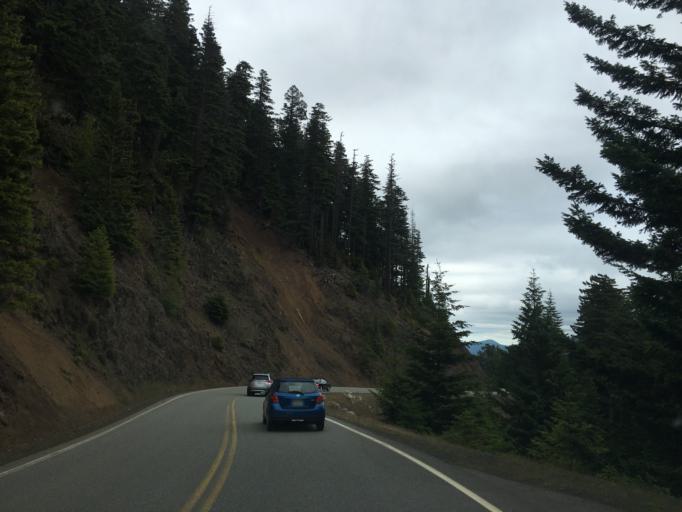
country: US
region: Washington
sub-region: Clallam County
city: Port Angeles East
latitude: 47.9963
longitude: -123.3827
